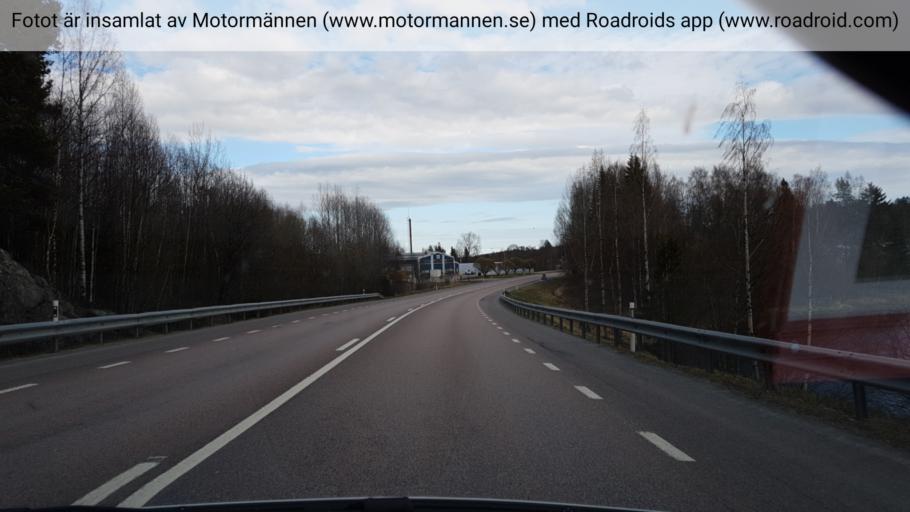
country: SE
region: Vaesternorrland
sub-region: Haernoesands Kommun
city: Haernoesand
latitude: 62.7926
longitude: 17.9070
